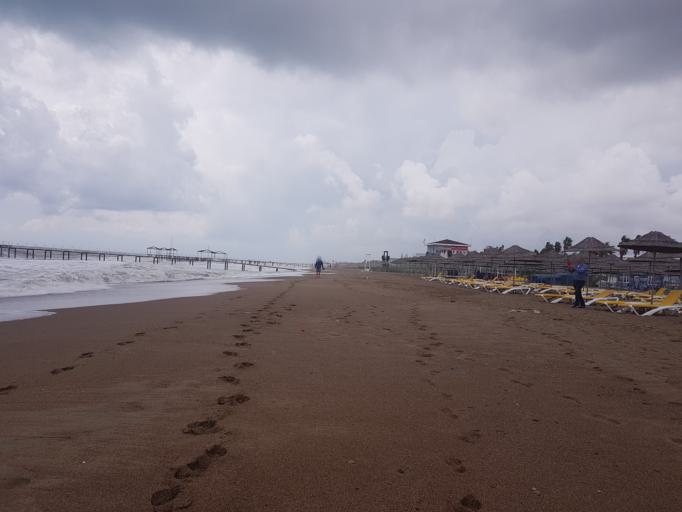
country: TR
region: Antalya
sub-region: Serik
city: Kumkoey
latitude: 36.8534
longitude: 30.8940
